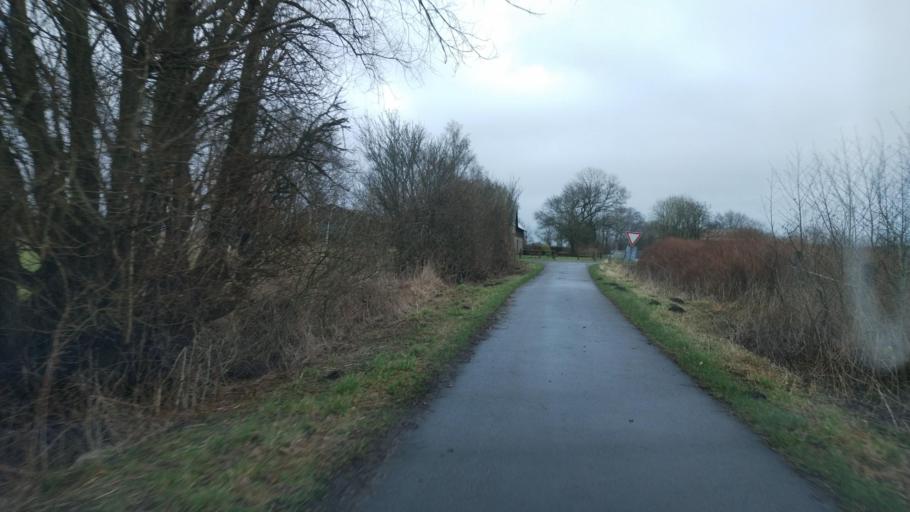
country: DE
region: Schleswig-Holstein
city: Hollingstedt
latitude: 54.4830
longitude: 9.3587
